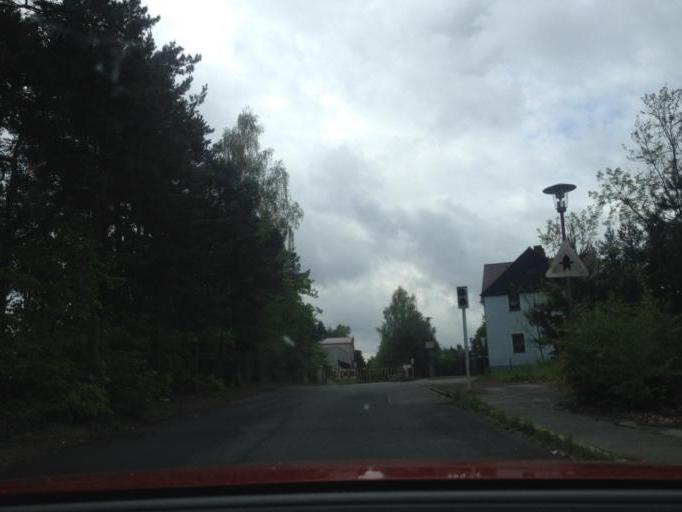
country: DE
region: Bavaria
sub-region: Regierungsbezirk Mittelfranken
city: Rothenbach an der Pegnitz
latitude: 49.4780
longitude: 11.2355
